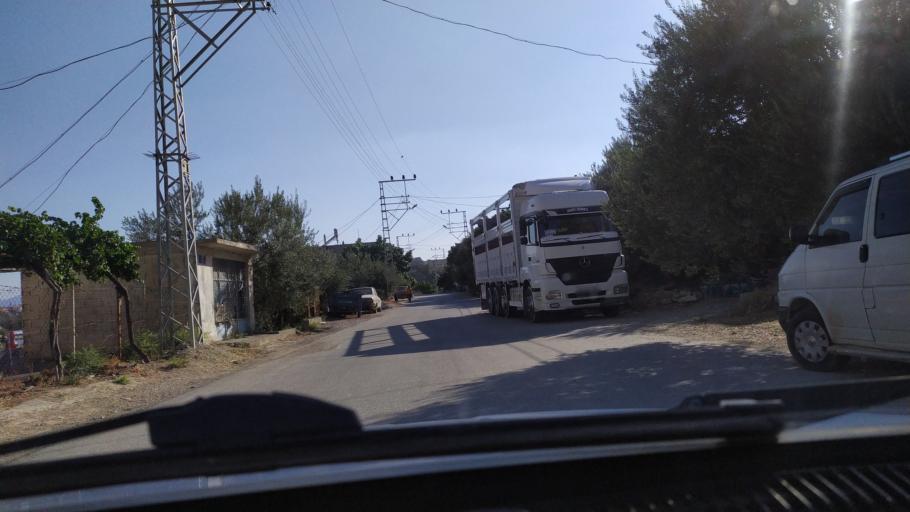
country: TR
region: Mersin
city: Mut
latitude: 36.6474
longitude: 33.4325
